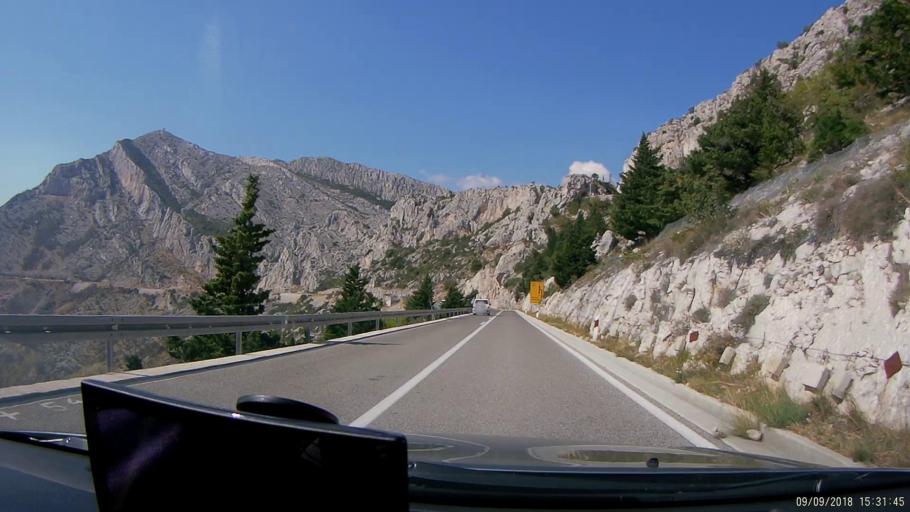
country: HR
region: Splitsko-Dalmatinska
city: Donja Brela
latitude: 43.4000
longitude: 16.8940
